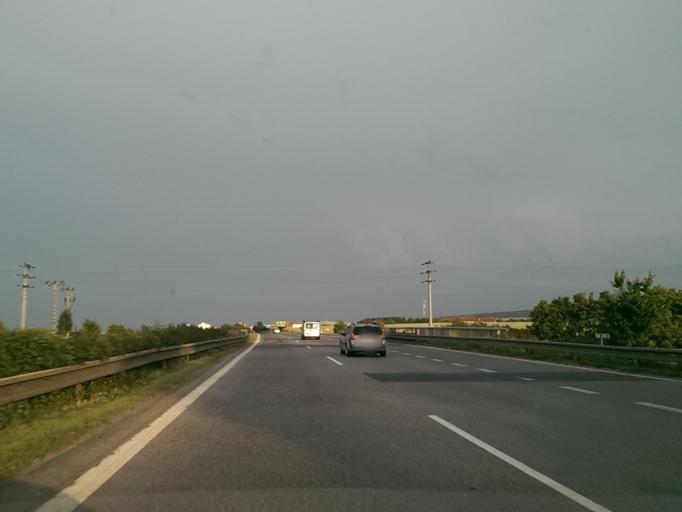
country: CZ
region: Central Bohemia
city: Zdiby
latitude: 50.1754
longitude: 14.4534
